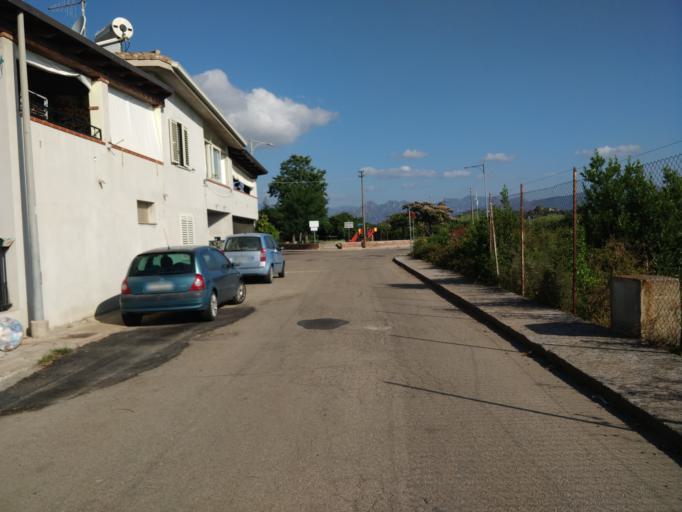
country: IT
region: Sardinia
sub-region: Provincia di Ogliastra
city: Girasole
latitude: 39.9538
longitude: 9.6635
